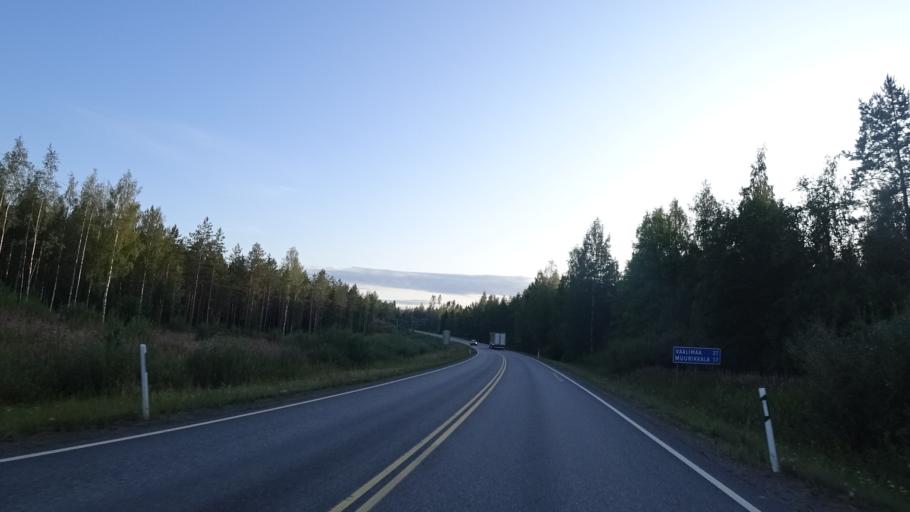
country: FI
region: South Karelia
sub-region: Lappeenranta
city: Ylaemaa
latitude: 60.7890
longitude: 28.0028
